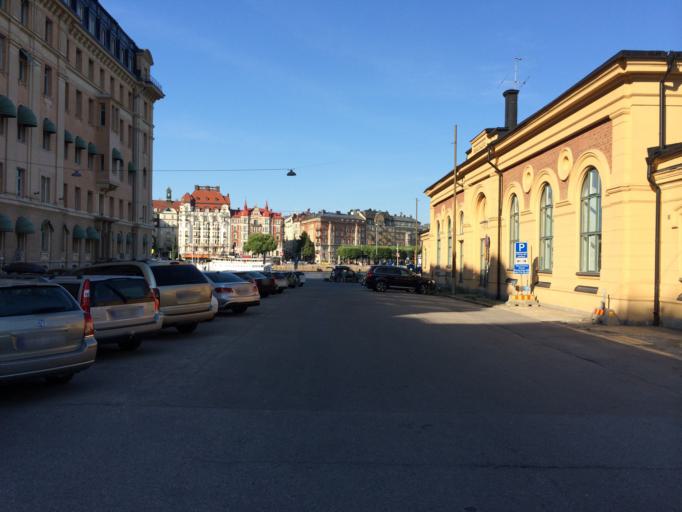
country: SE
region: Stockholm
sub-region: Stockholms Kommun
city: OEstermalm
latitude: 59.3296
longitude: 18.0782
